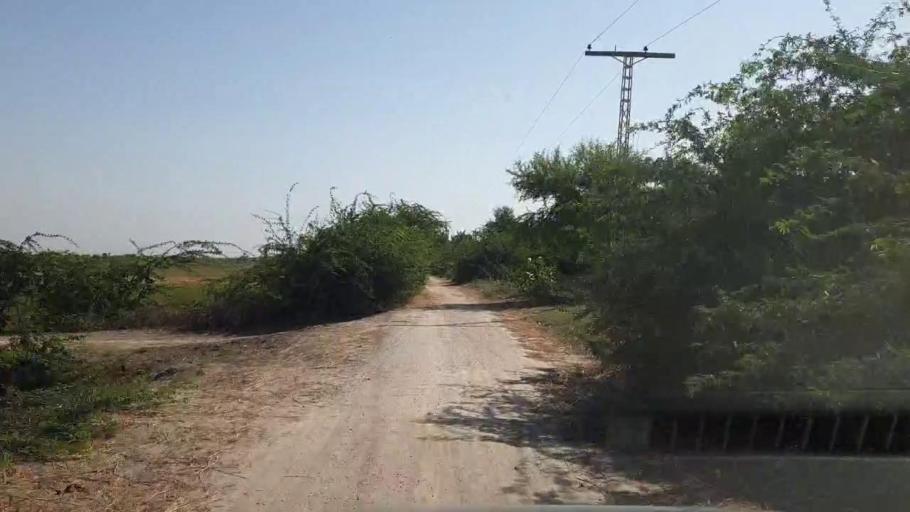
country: PK
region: Sindh
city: Tando Bago
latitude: 24.6423
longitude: 68.9885
